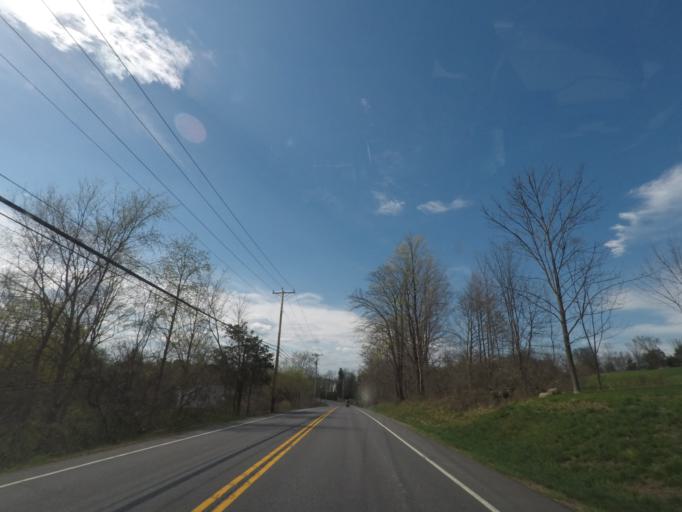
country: US
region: New York
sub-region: Greene County
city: Cairo
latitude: 42.3428
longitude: -74.0305
